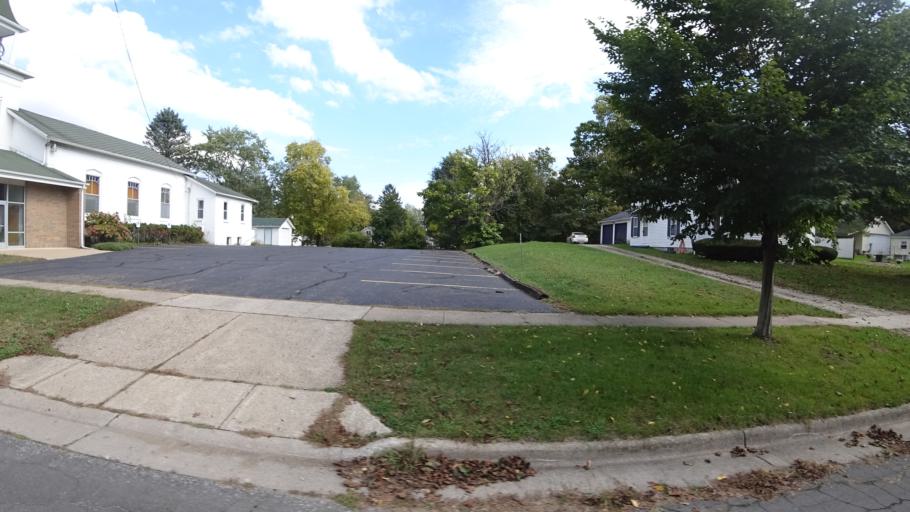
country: US
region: Michigan
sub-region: Saint Joseph County
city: Three Rivers
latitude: 41.9355
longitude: -85.6235
